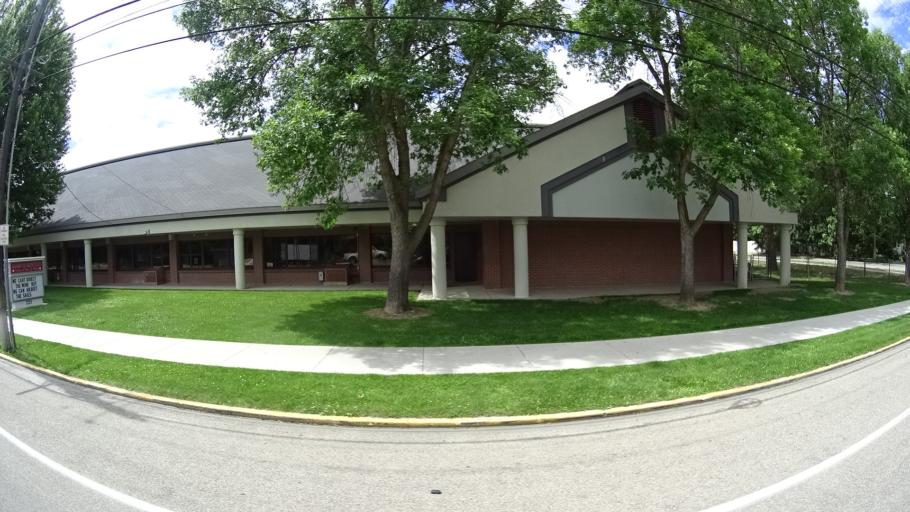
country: US
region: Idaho
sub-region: Ada County
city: Boise
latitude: 43.6034
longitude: -116.1741
